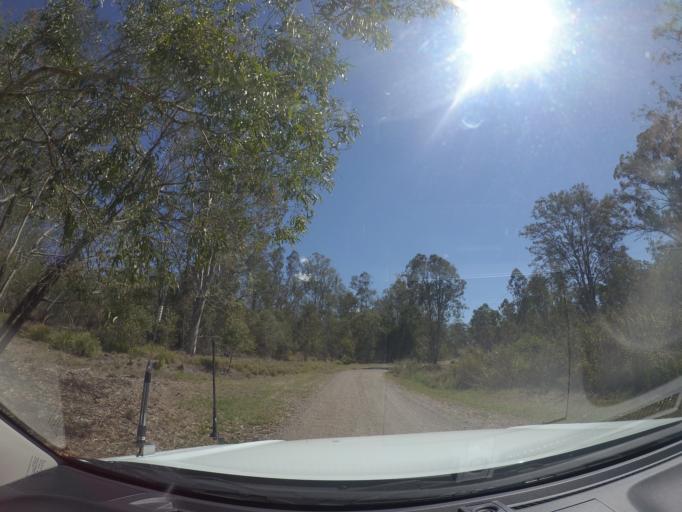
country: AU
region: Queensland
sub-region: Ipswich
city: Springfield Lakes
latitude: -27.7435
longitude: 152.9391
